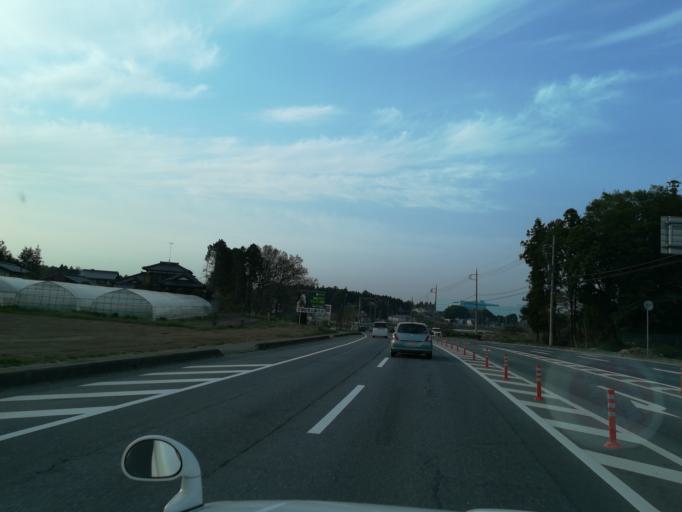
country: JP
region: Ibaraki
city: Naka
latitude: 36.0594
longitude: 140.0836
